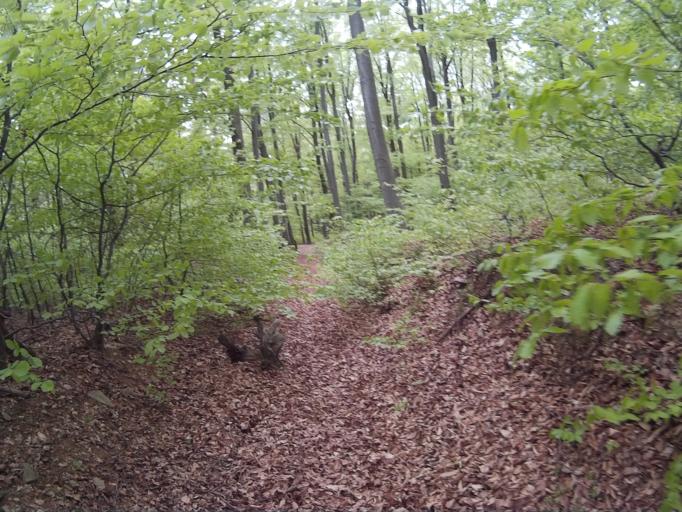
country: HU
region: Vas
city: Koszeg
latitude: 47.3578
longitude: 16.4911
